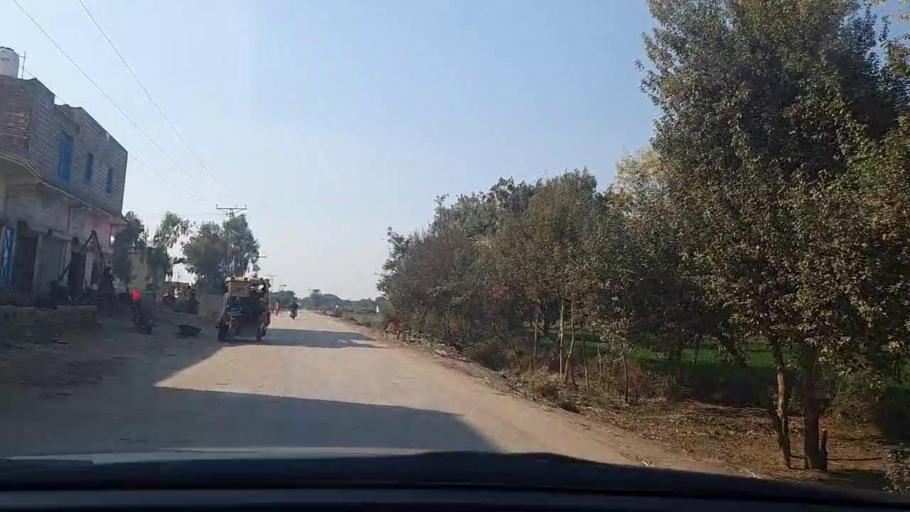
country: PK
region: Sindh
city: Daulatpur
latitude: 26.3039
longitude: 68.0930
